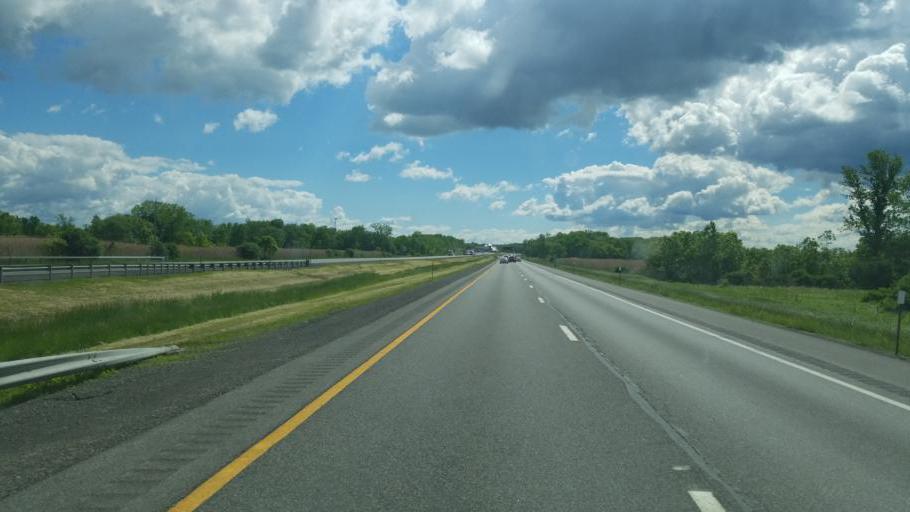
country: US
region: New York
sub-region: Madison County
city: Bolivar
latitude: 43.0955
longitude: -75.8561
